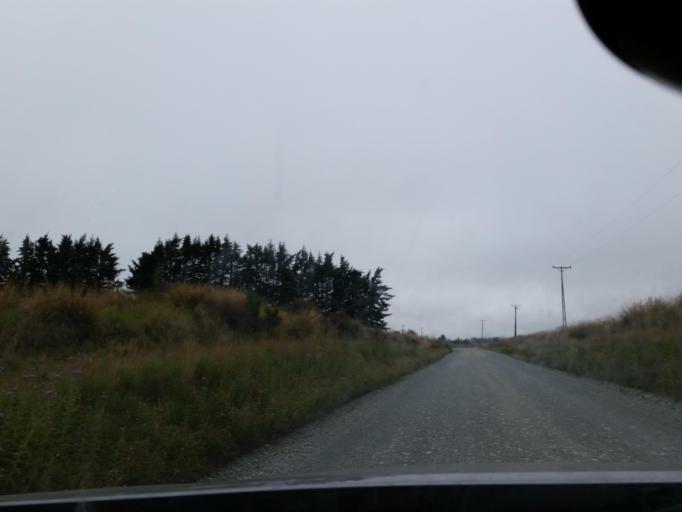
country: NZ
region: Southland
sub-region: Southland District
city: Te Anau
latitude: -45.5085
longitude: 168.1150
